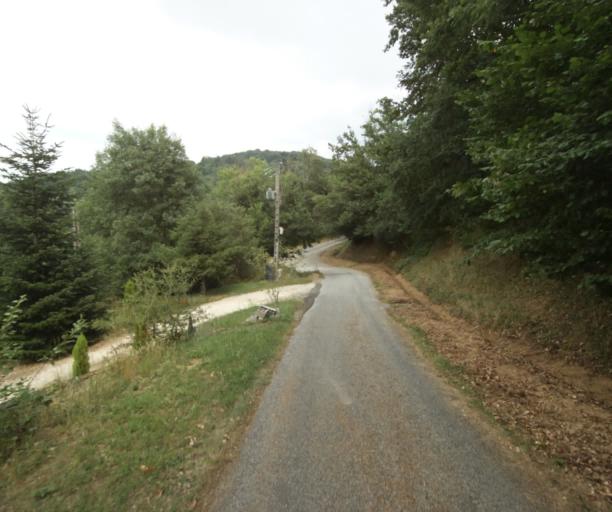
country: FR
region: Midi-Pyrenees
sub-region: Departement du Tarn
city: Soreze
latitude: 43.4322
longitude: 2.0451
